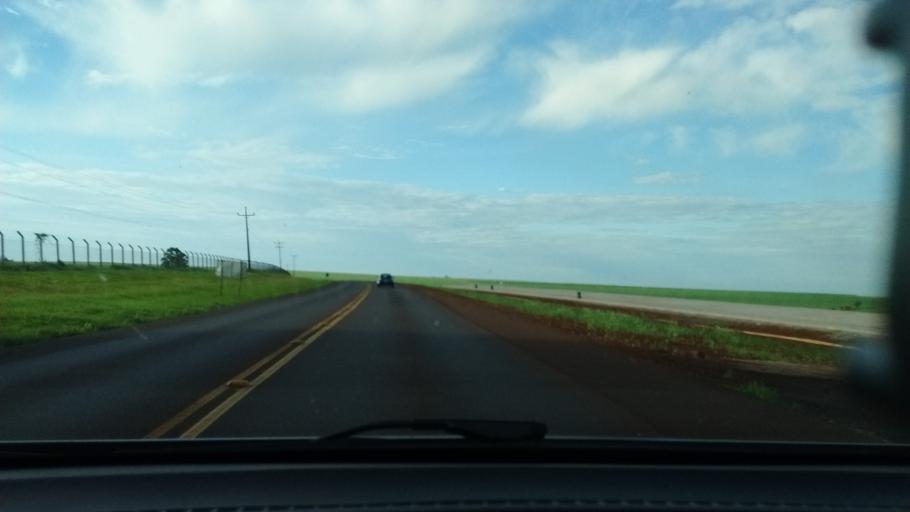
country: BR
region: Parana
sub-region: Cascavel
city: Cascavel
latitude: -25.0934
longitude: -53.5937
